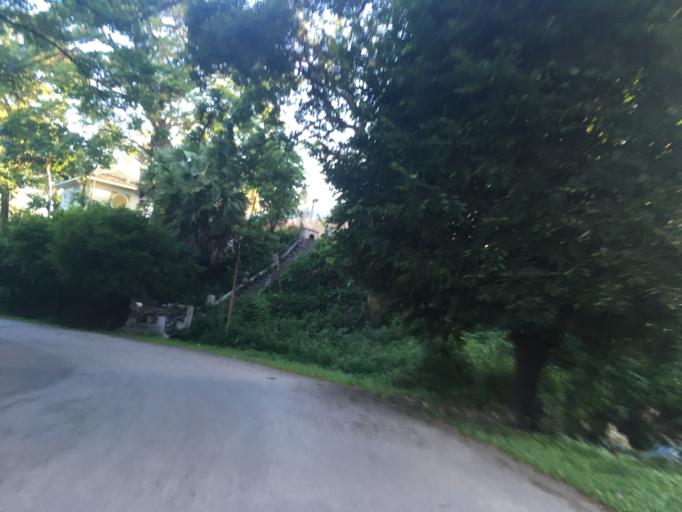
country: MM
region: Mon
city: Mawlamyine
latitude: 16.4855
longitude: 97.6282
